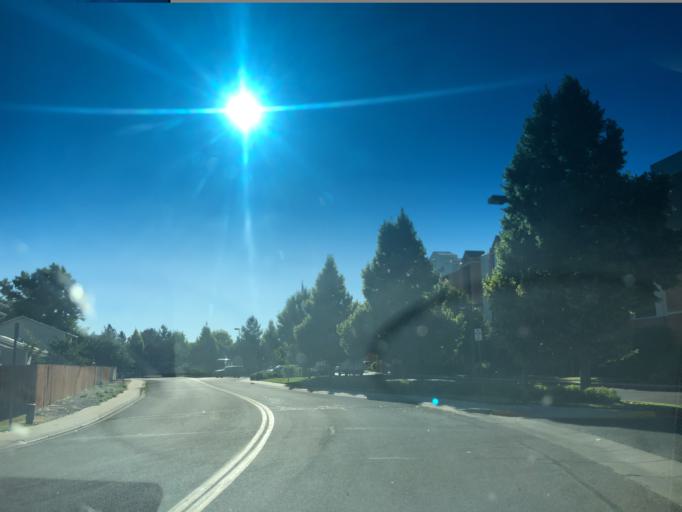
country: US
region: Idaho
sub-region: Ada County
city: Garden City
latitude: 43.6128
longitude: -116.2846
